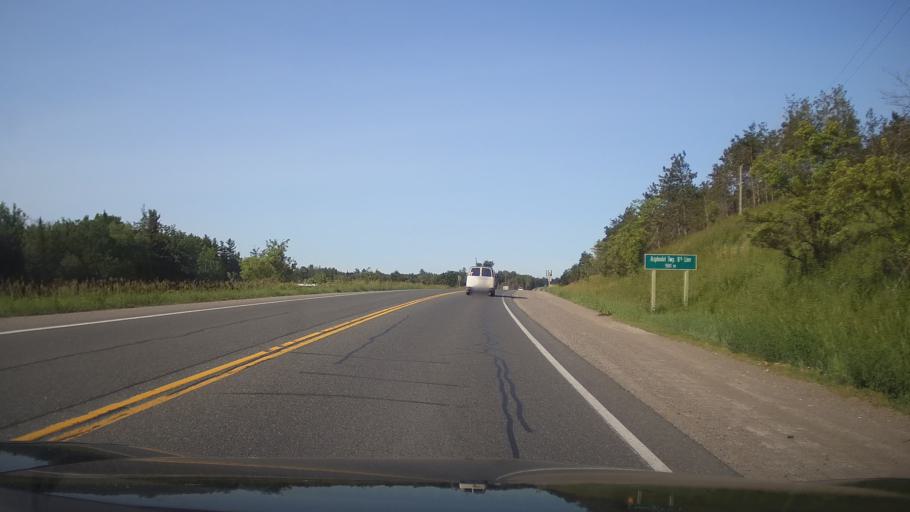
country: CA
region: Ontario
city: Peterborough
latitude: 44.3752
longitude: -77.9870
